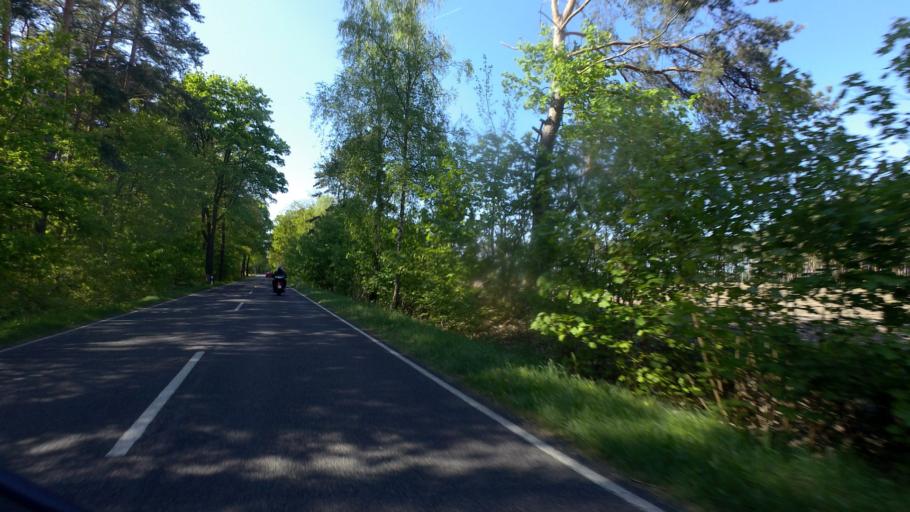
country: DE
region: Brandenburg
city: Bestensee
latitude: 52.2237
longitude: 13.6792
